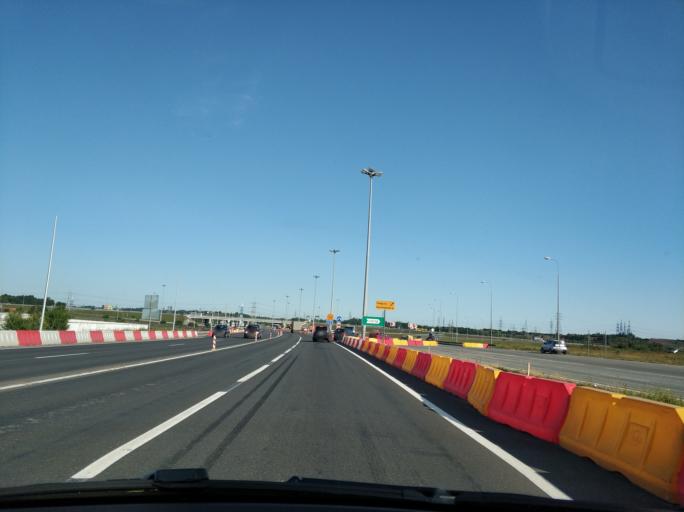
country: RU
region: Leningrad
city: Bugry
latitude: 60.0882
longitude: 30.3744
